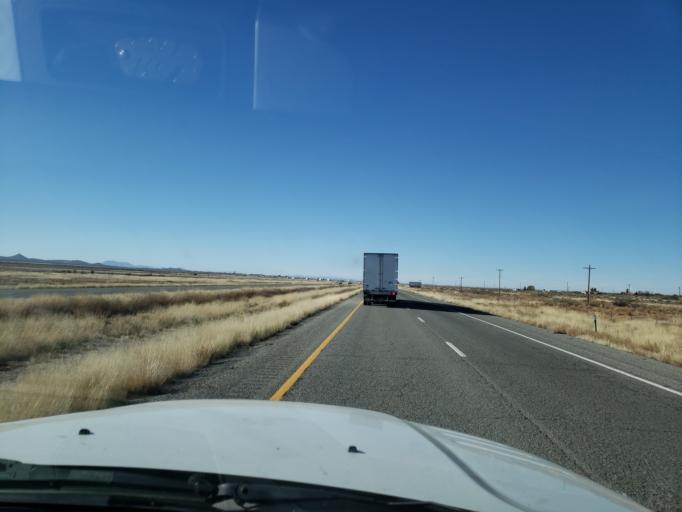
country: US
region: New Mexico
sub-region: Hidalgo County
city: Lordsburg
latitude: 32.3242
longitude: -108.6273
